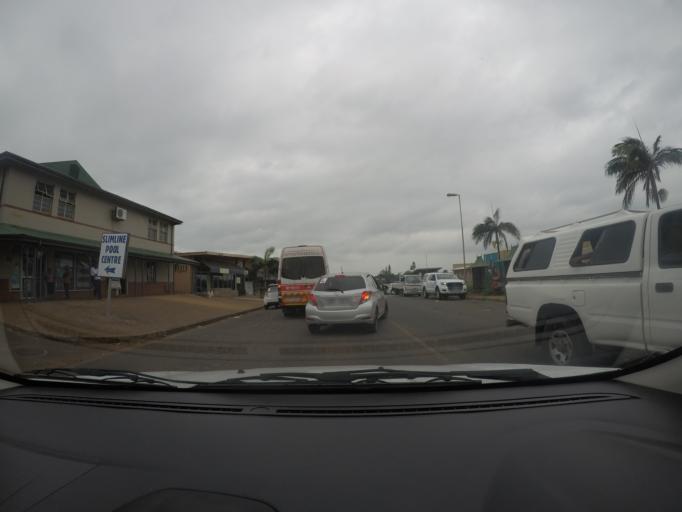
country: ZA
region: KwaZulu-Natal
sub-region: uThungulu District Municipality
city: Empangeni
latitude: -28.7398
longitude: 31.8952
